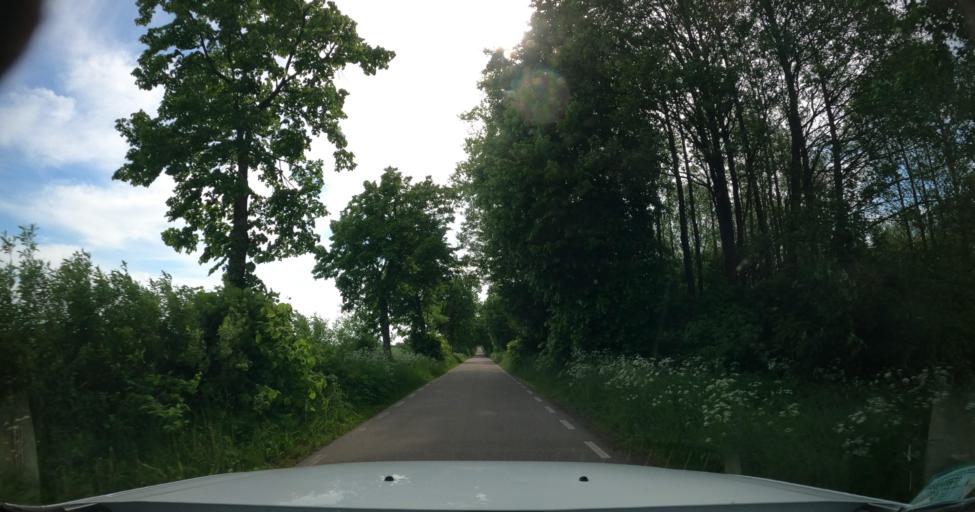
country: PL
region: Warmian-Masurian Voivodeship
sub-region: Powiat lidzbarski
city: Lubomino
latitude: 54.0571
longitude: 20.1767
